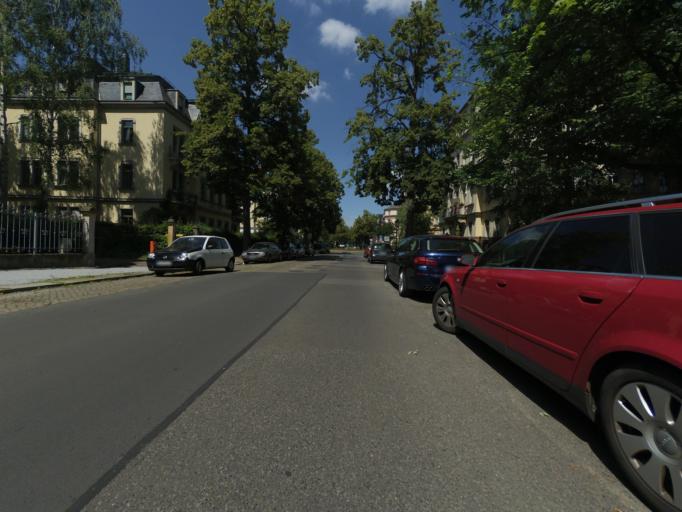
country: DE
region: Saxony
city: Albertstadt
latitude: 51.0473
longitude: 13.7935
